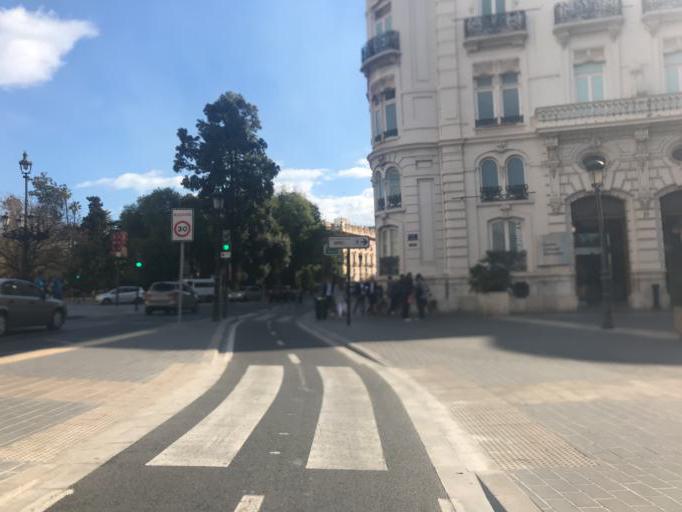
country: ES
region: Valencia
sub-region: Provincia de Valencia
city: Valencia
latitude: 39.4742
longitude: -0.3699
